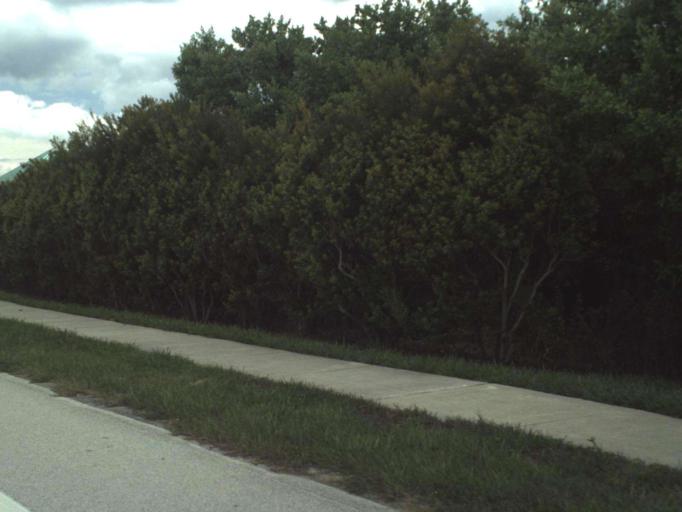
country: US
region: Florida
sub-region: Martin County
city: Jensen Beach
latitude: 27.2502
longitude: -80.1949
